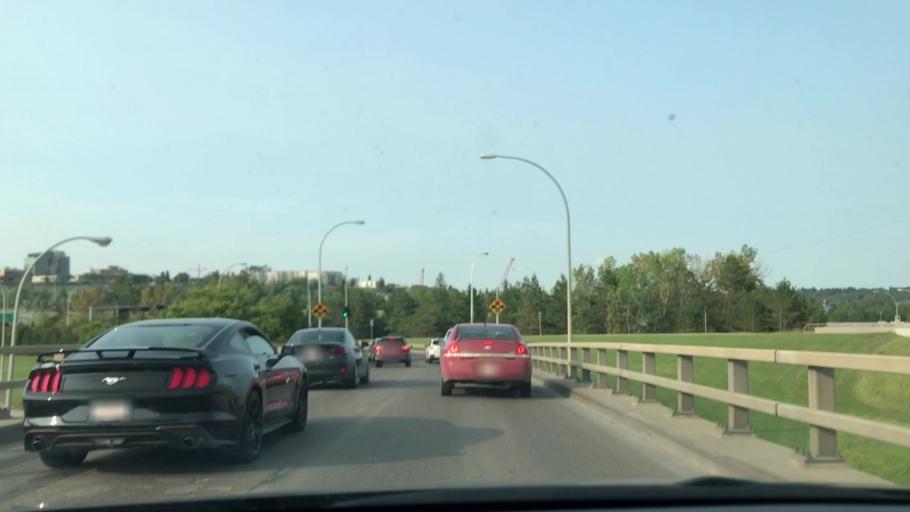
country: CA
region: Alberta
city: Edmonton
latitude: 53.5337
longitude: -113.4837
